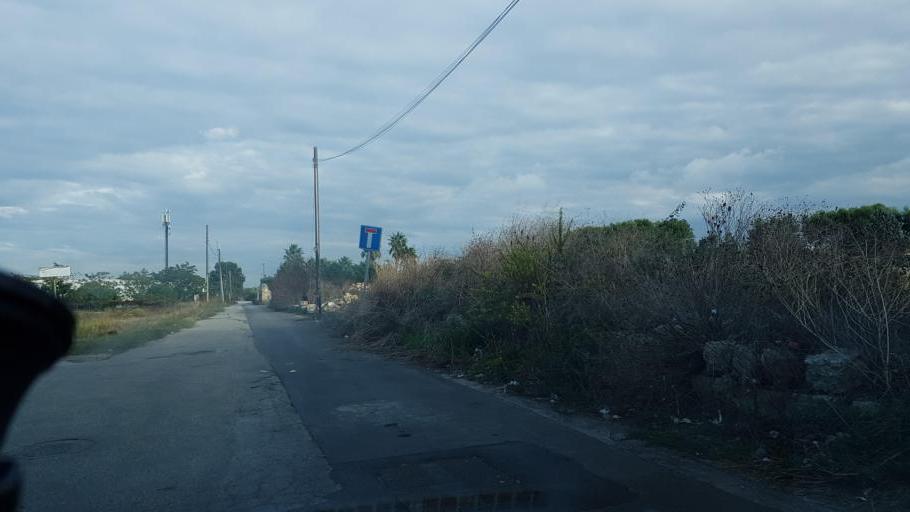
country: IT
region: Apulia
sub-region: Provincia di Brindisi
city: Francavilla Fontana
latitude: 40.5353
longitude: 17.5890
